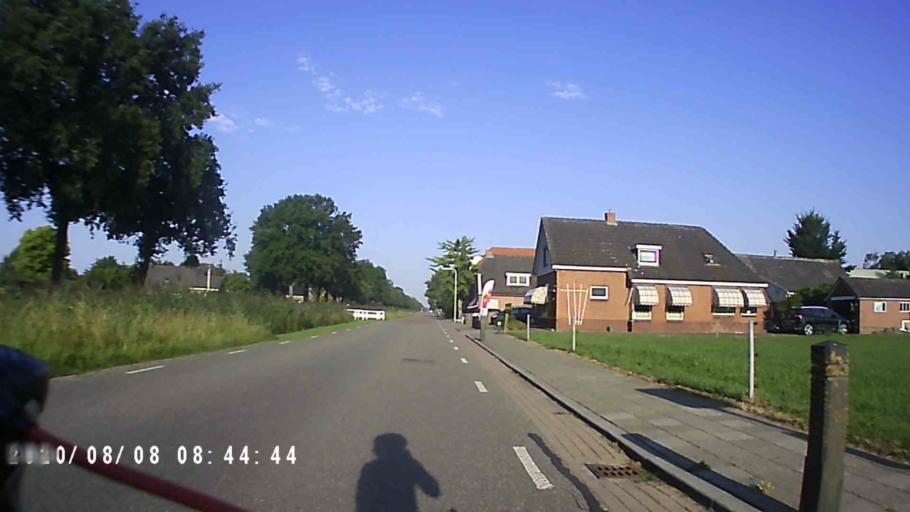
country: NL
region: Groningen
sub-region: Gemeente Leek
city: Leek
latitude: 53.0649
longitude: 6.3583
